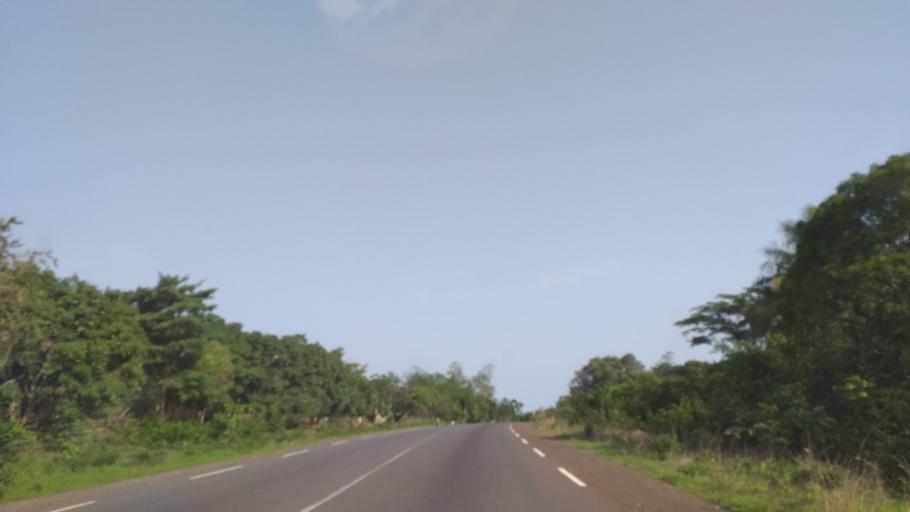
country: GN
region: Boke
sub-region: Boffa
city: Boffa
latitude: 10.2899
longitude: -14.1903
